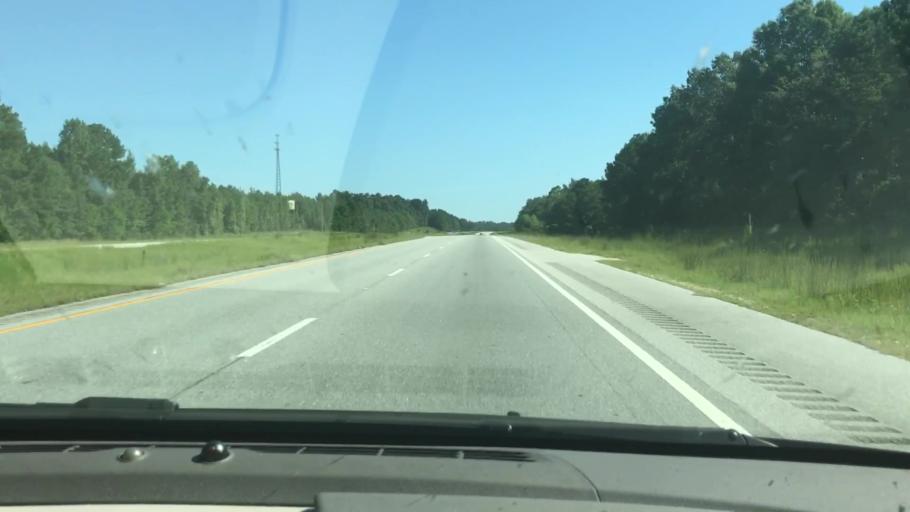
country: US
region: Alabama
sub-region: Russell County
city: Ladonia
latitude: 32.3838
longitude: -85.0813
